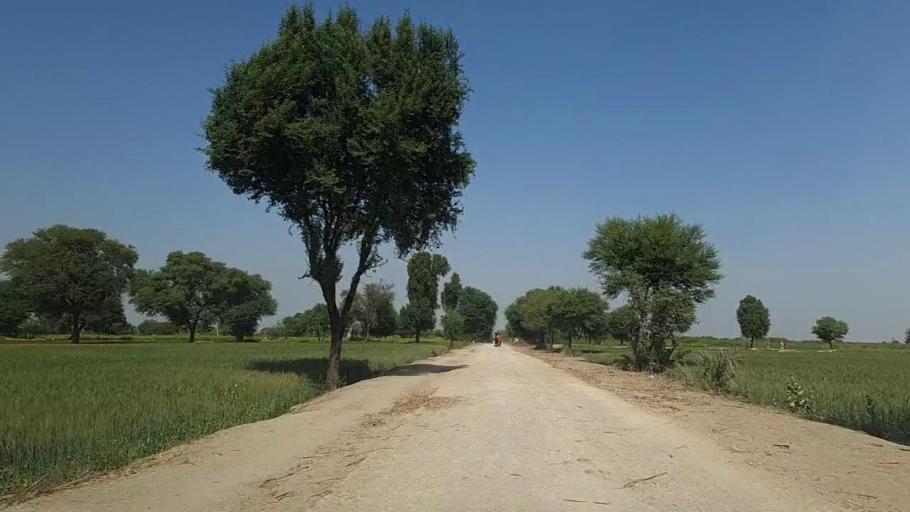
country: PK
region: Sindh
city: Samaro
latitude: 25.1831
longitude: 69.4040
